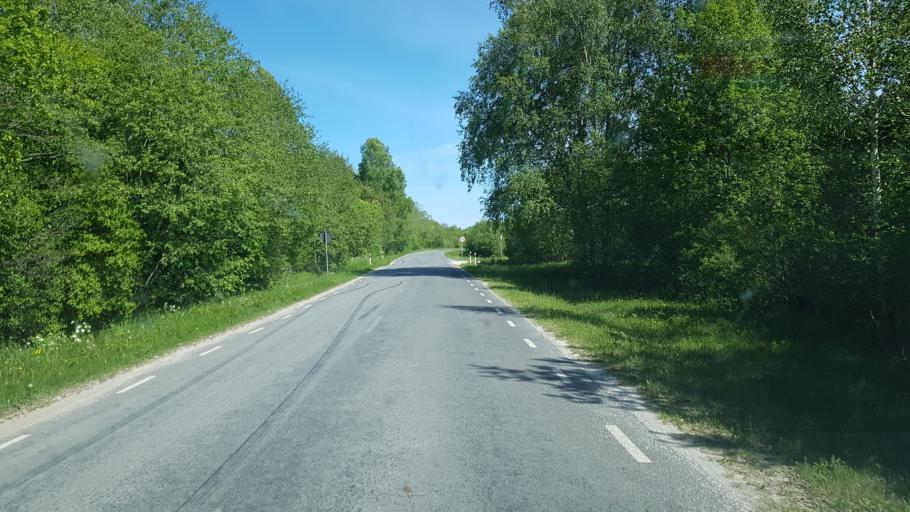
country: EE
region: Saare
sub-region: Kuressaare linn
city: Kuressaare
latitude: 58.2769
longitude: 22.5009
